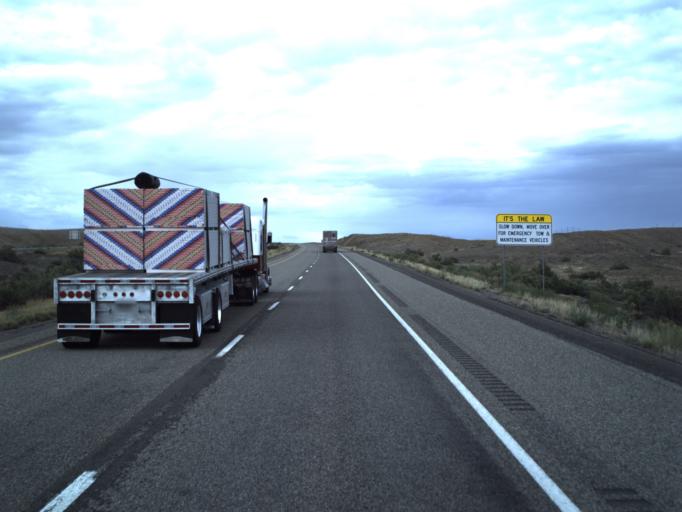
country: US
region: Colorado
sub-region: Mesa County
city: Loma
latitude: 39.1255
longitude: -109.1670
